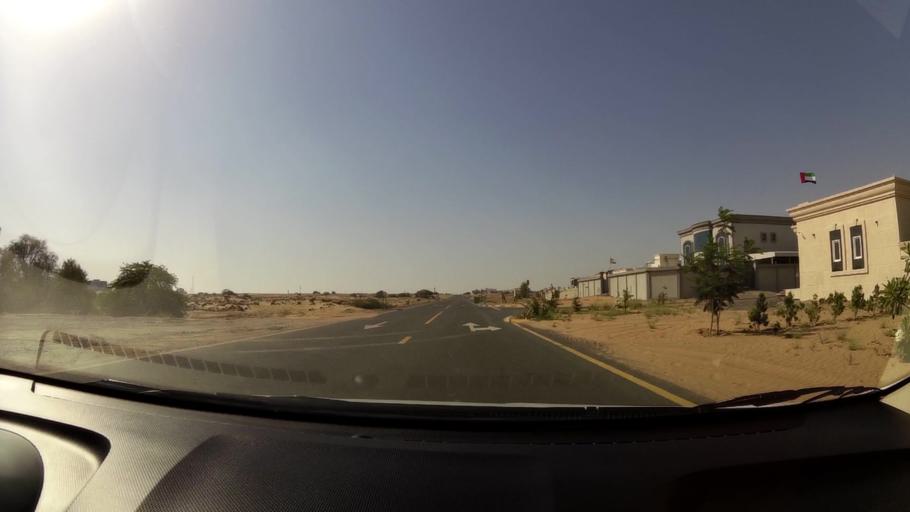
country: AE
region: Umm al Qaywayn
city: Umm al Qaywayn
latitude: 25.4761
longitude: 55.5956
